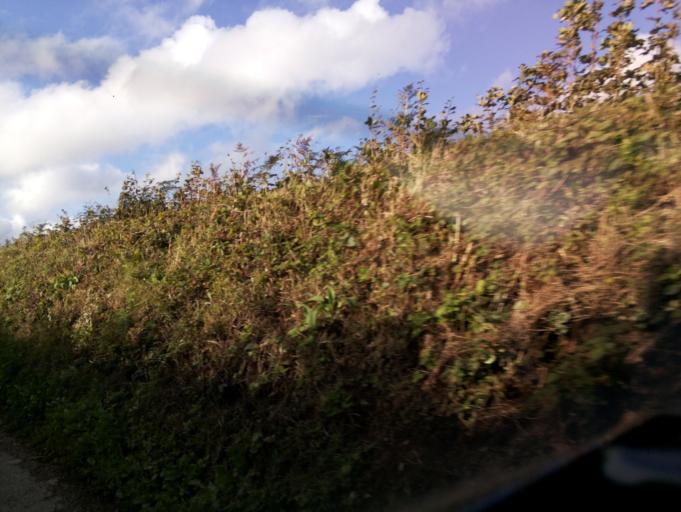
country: GB
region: England
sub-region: Devon
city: Dartmouth
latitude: 50.3457
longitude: -3.6112
